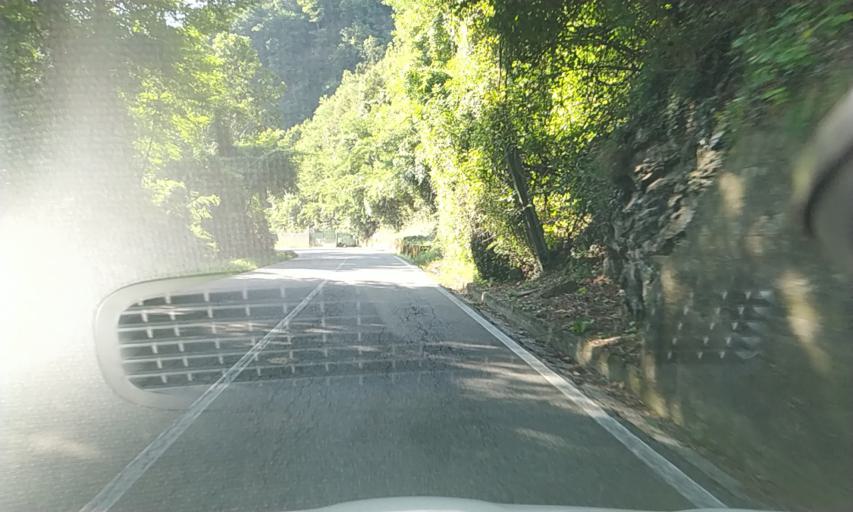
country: IT
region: Piedmont
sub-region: Provincia di Vercelli
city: Varallo
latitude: 45.8010
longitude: 8.2613
